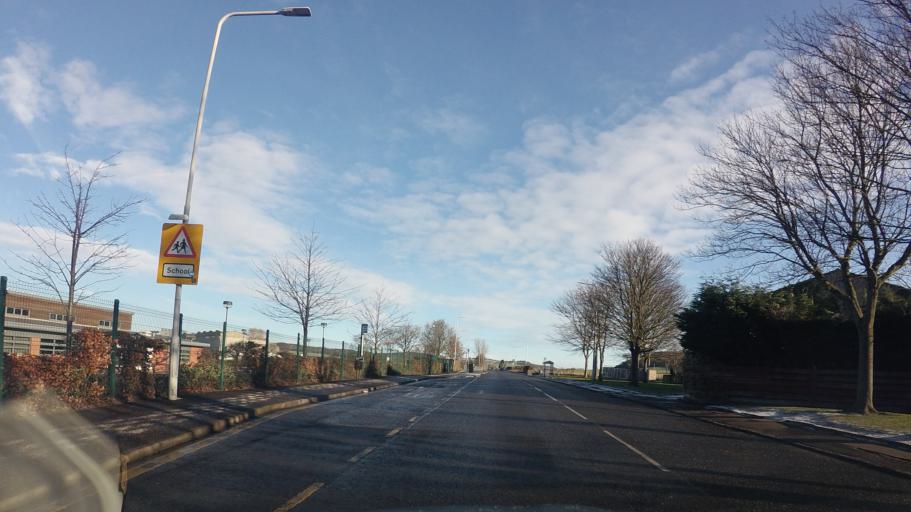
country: GB
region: Scotland
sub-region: Fife
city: Inverkeithing
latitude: 56.0342
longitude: -3.3874
